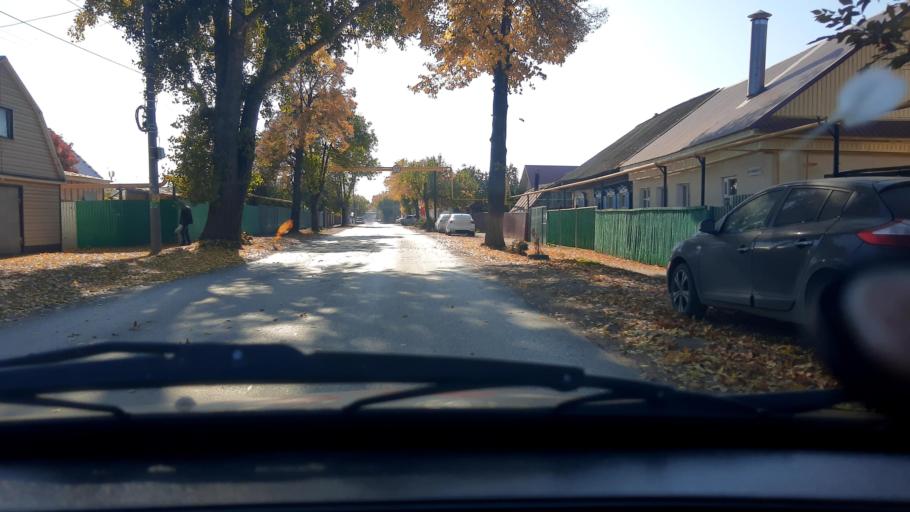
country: RU
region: Bashkortostan
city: Mikhaylovka
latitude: 54.7398
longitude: 55.8994
